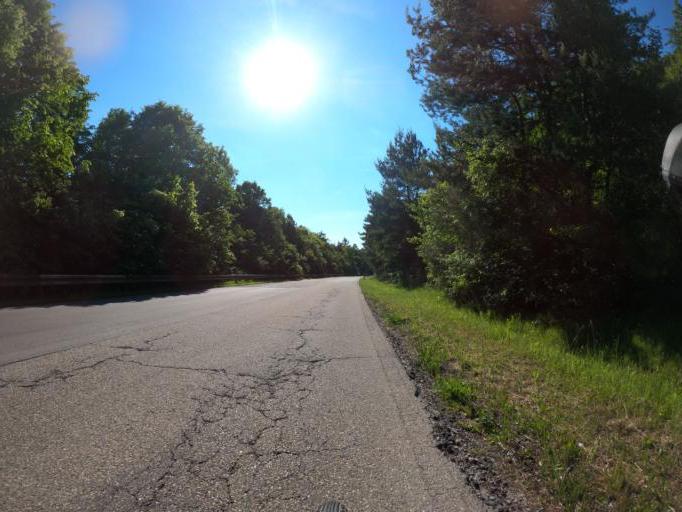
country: DE
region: Baden-Wuerttemberg
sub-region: Regierungsbezirk Stuttgart
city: Sindelfingen
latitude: 48.7457
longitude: 9.0317
